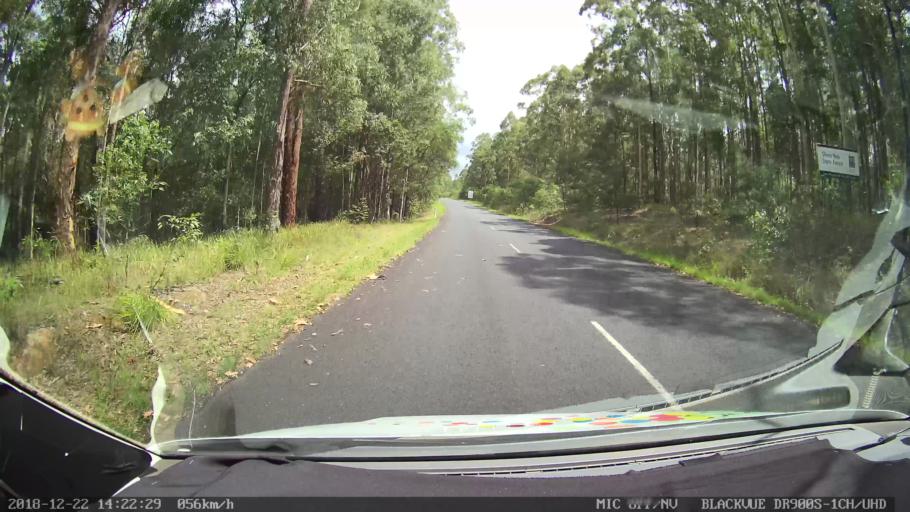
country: AU
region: New South Wales
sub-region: Clarence Valley
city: Coutts Crossing
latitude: -30.0263
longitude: 152.6535
